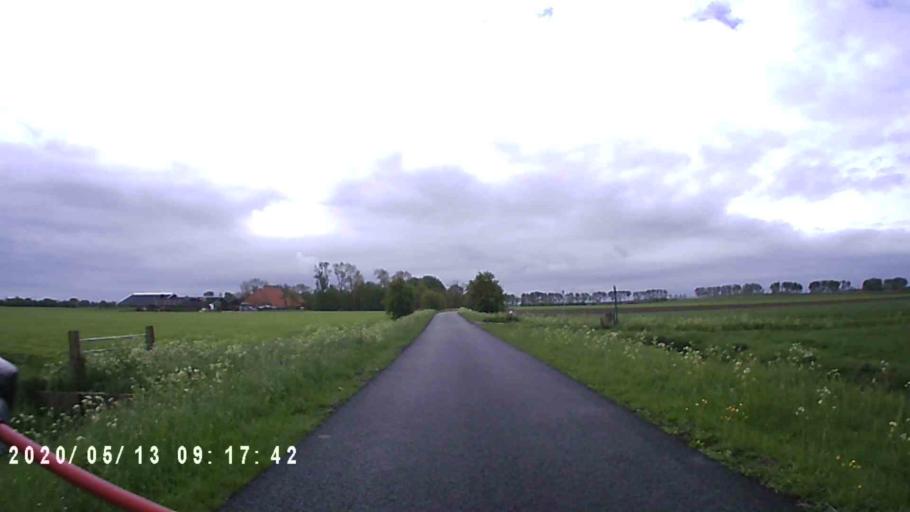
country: NL
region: Groningen
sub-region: Gemeente Zuidhorn
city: Noordhorn
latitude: 53.2675
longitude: 6.4150
